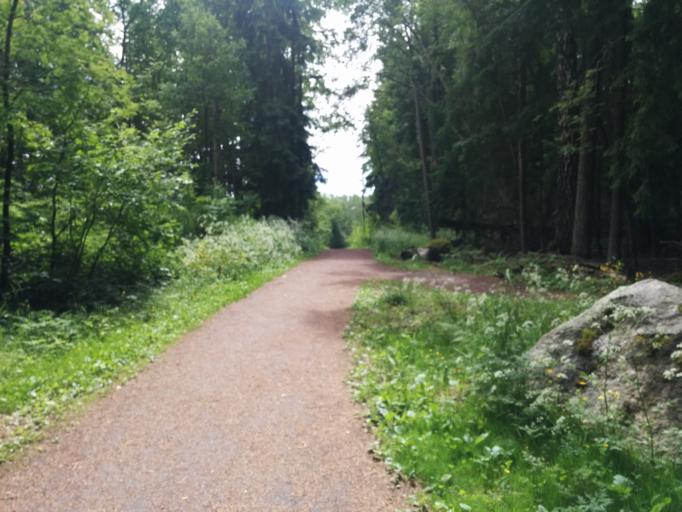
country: FI
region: Uusimaa
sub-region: Helsinki
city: Vantaa
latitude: 60.2394
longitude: 25.1284
